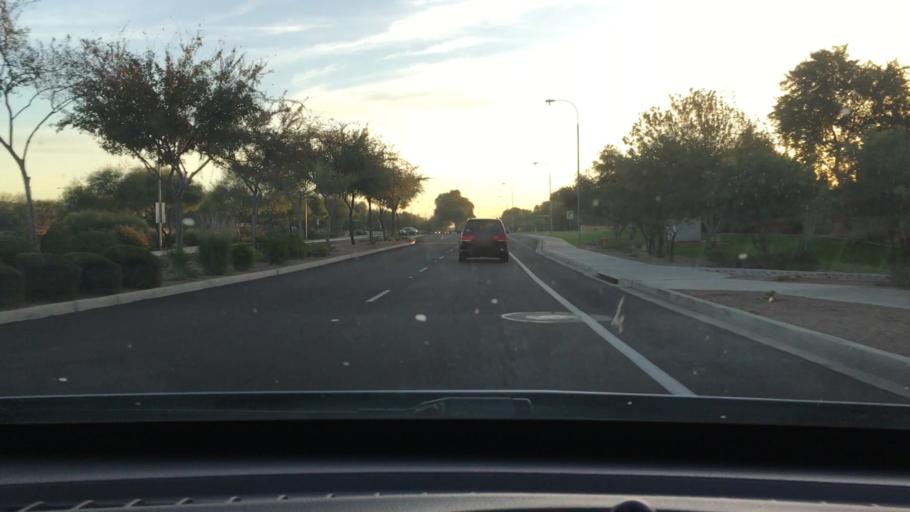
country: US
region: Arizona
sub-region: Maricopa County
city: Chandler
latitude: 33.2336
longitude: -111.7831
